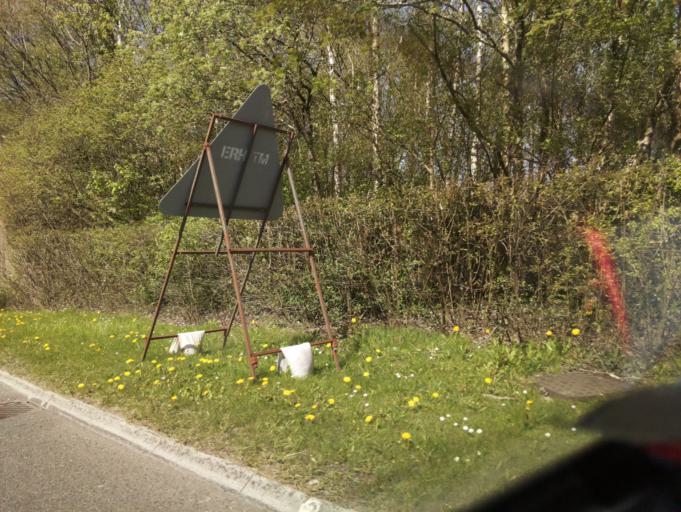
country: GB
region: Wales
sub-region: Rhondda Cynon Taf
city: Cwmbach
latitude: 51.7033
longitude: -3.4275
